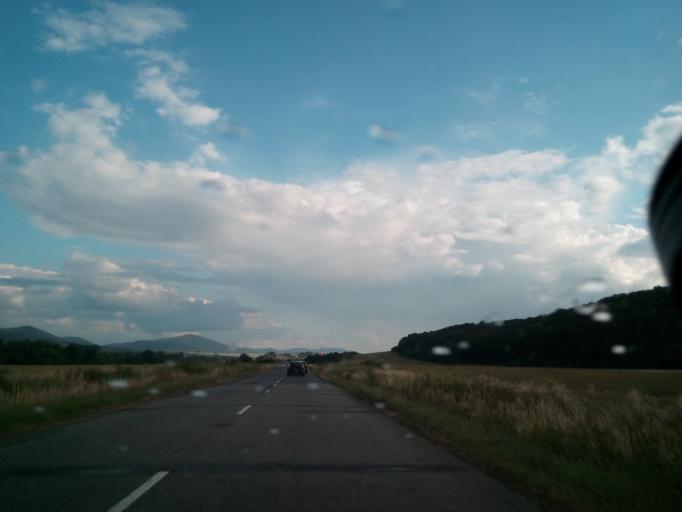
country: SK
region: Kosicky
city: Kosice
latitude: 48.6520
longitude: 21.3757
